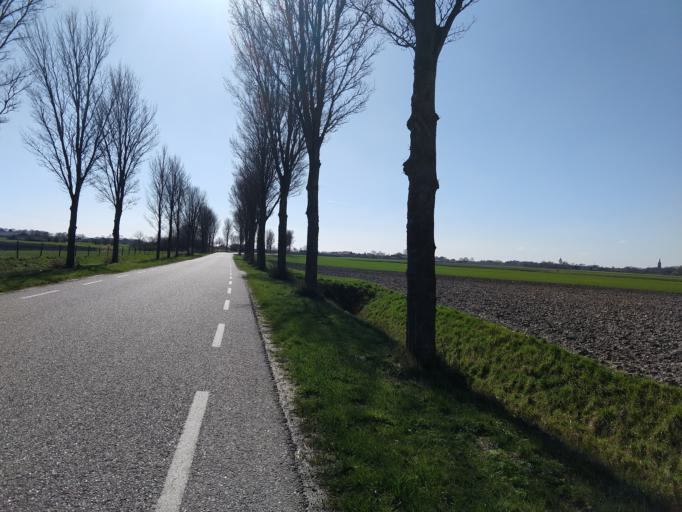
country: NL
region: Zeeland
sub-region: Gemeente Goes
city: Goes
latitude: 51.4996
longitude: 3.9469
